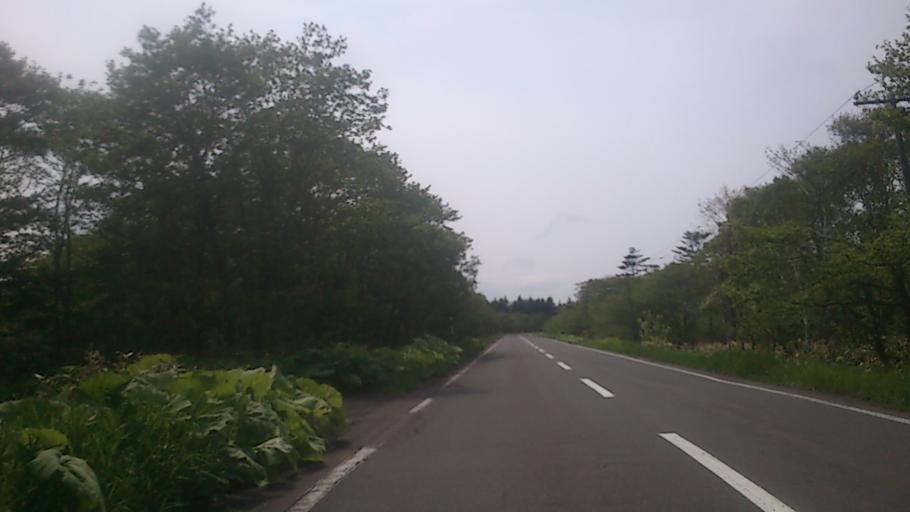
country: JP
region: Hokkaido
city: Nemuro
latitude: 43.2059
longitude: 145.3505
